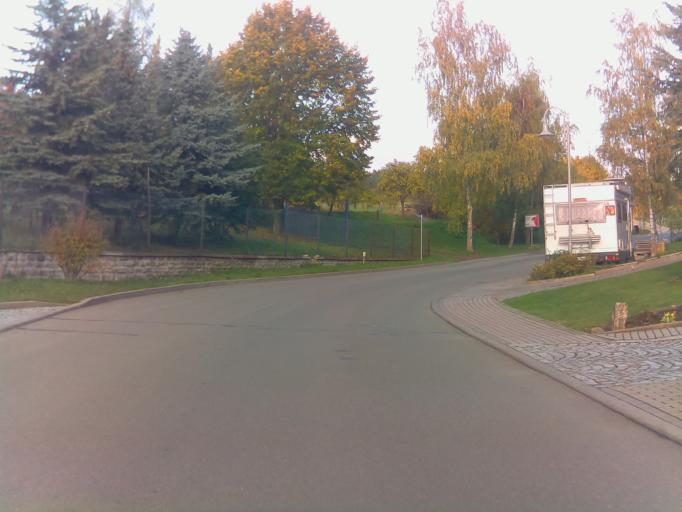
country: DE
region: Thuringia
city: Elleben
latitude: 50.8803
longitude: 11.0858
